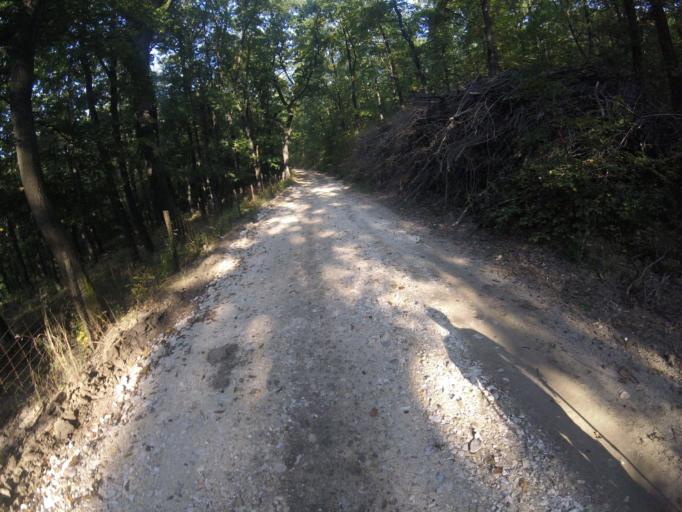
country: HU
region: Komarom-Esztergom
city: Piliscsev
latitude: 47.6892
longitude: 18.8507
